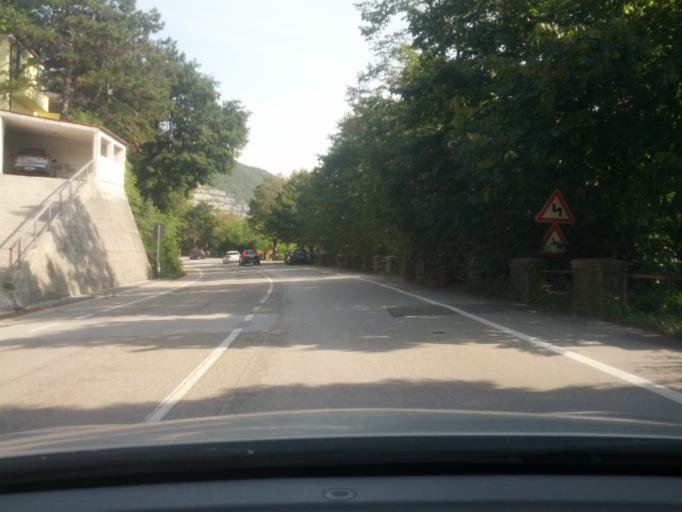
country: IT
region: Friuli Venezia Giulia
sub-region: Provincia di Trieste
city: Villa Opicina
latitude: 45.6661
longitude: 13.7993
